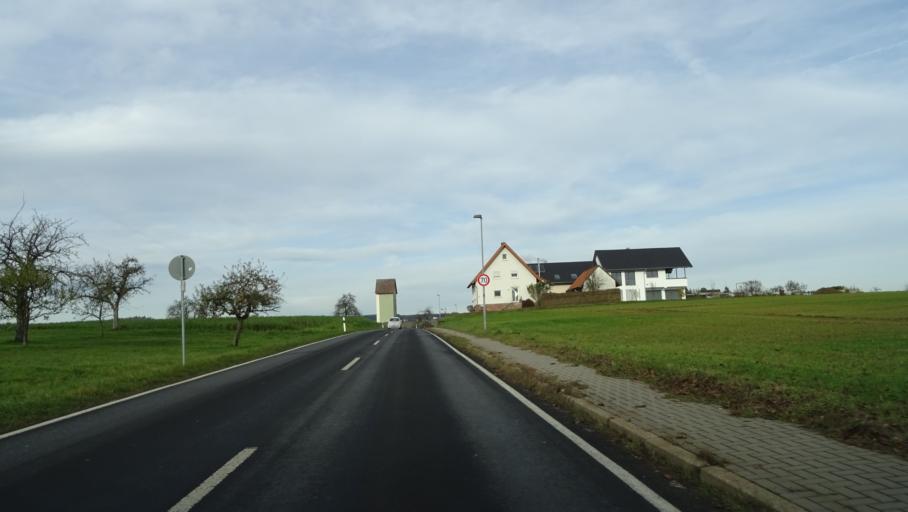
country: DE
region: Baden-Wuerttemberg
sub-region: Karlsruhe Region
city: Fahrenbach
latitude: 49.4089
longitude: 9.1578
